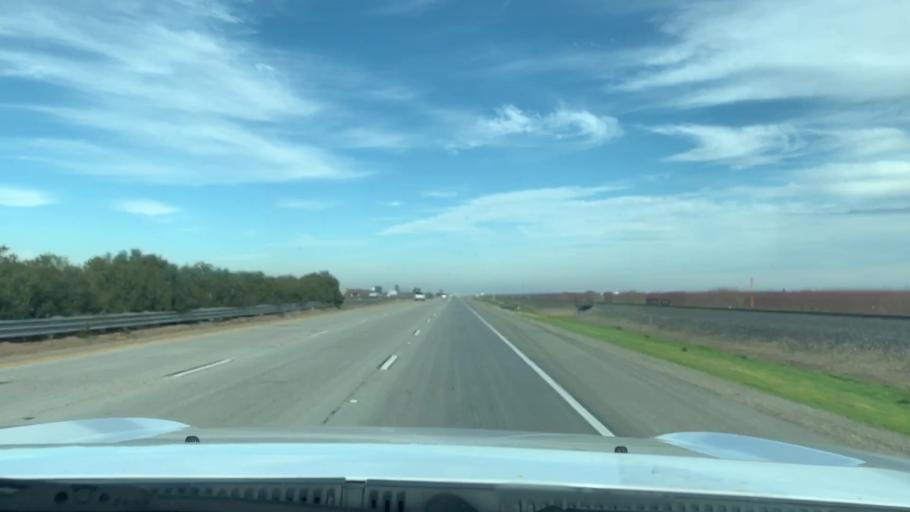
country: US
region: California
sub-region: Kern County
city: McFarland
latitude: 35.6186
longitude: -119.2126
